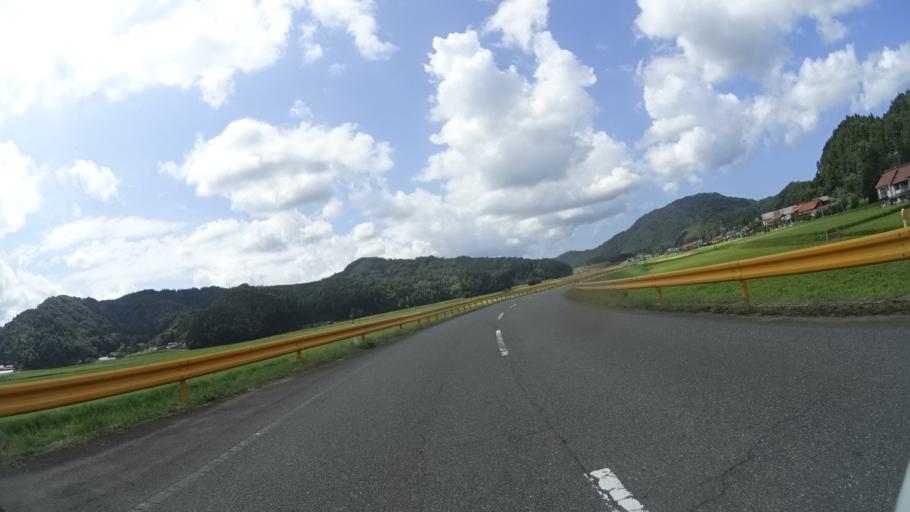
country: JP
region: Yamaguchi
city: Hagi
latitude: 34.5155
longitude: 131.6070
